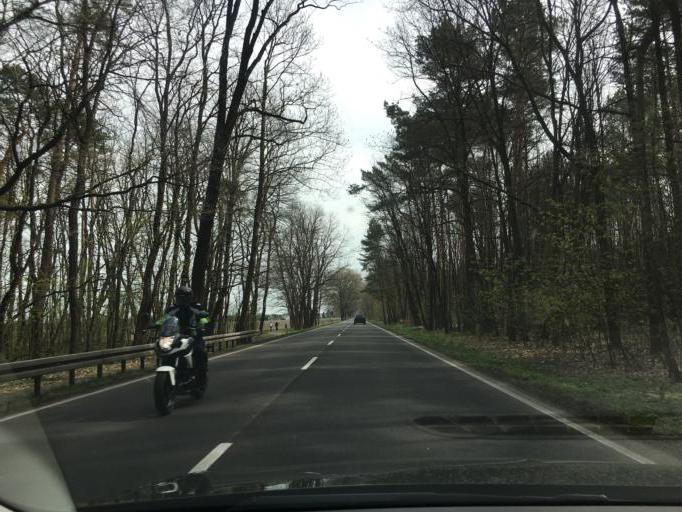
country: DE
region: Brandenburg
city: Spremberg
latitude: 51.5698
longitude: 14.4529
